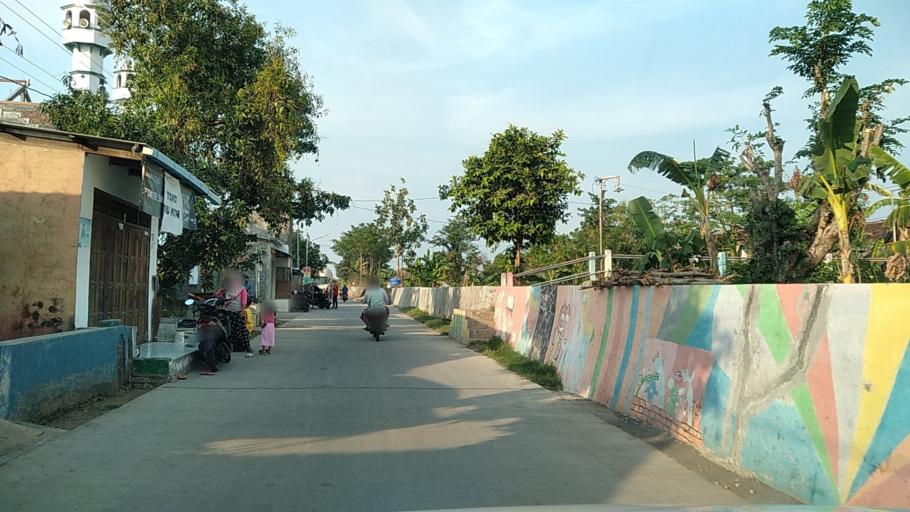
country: ID
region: Central Java
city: Semarang
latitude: -6.9592
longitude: 110.3030
